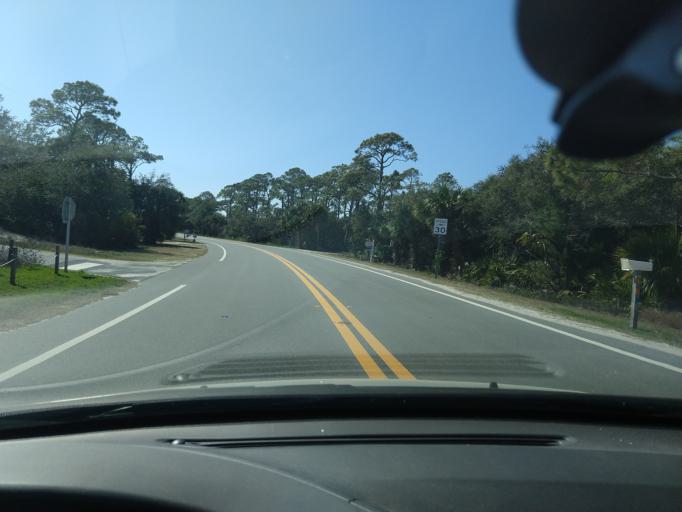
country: US
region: Florida
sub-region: Gulf County
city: Port Saint Joe
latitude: 29.6815
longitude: -85.2262
